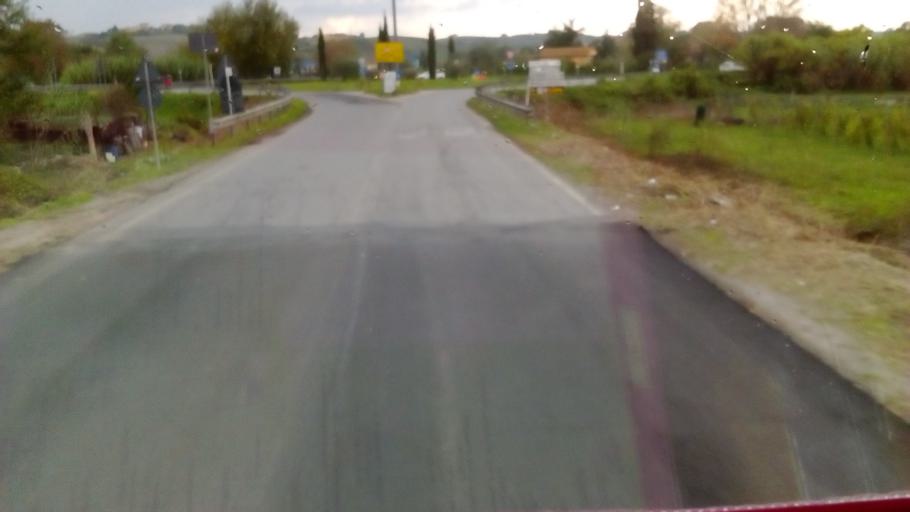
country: IT
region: Tuscany
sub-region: Province of Florence
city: Castelfiorentino
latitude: 43.5926
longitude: 10.9735
